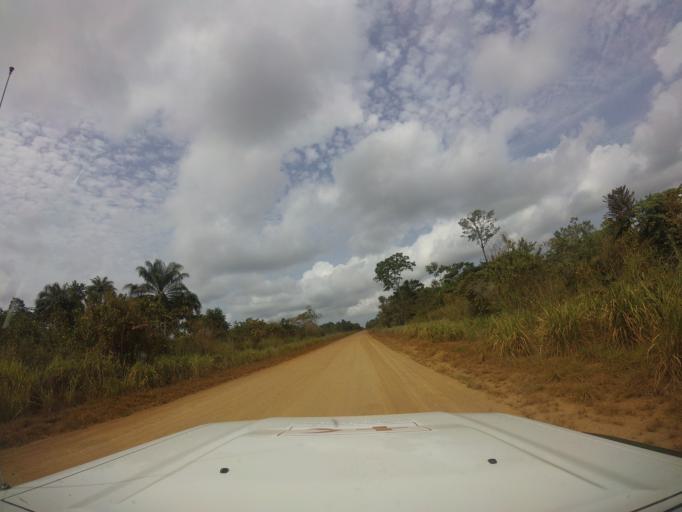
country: LR
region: Grand Cape Mount
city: Robertsport
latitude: 6.6888
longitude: -11.1164
